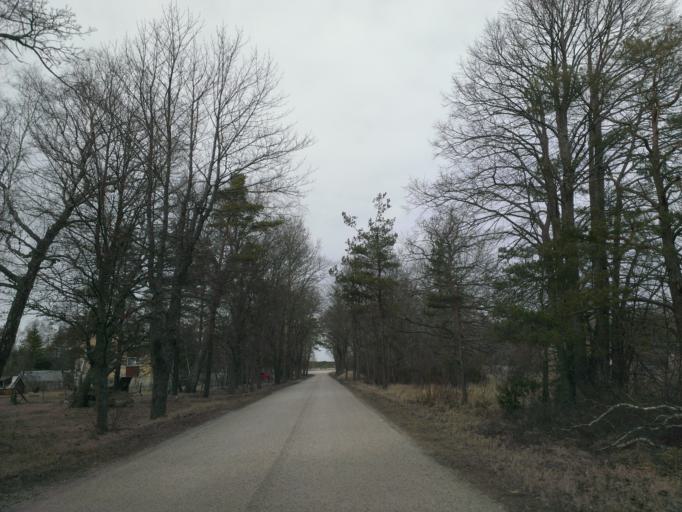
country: EE
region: Laeaene
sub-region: Lihula vald
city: Lihula
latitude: 58.5880
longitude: 23.5373
